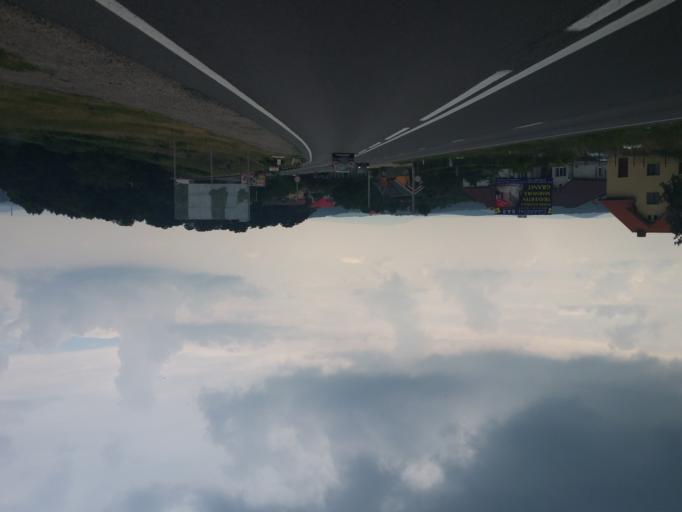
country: RO
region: Salaj
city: Zalau
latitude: 47.1614
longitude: 23.0875
